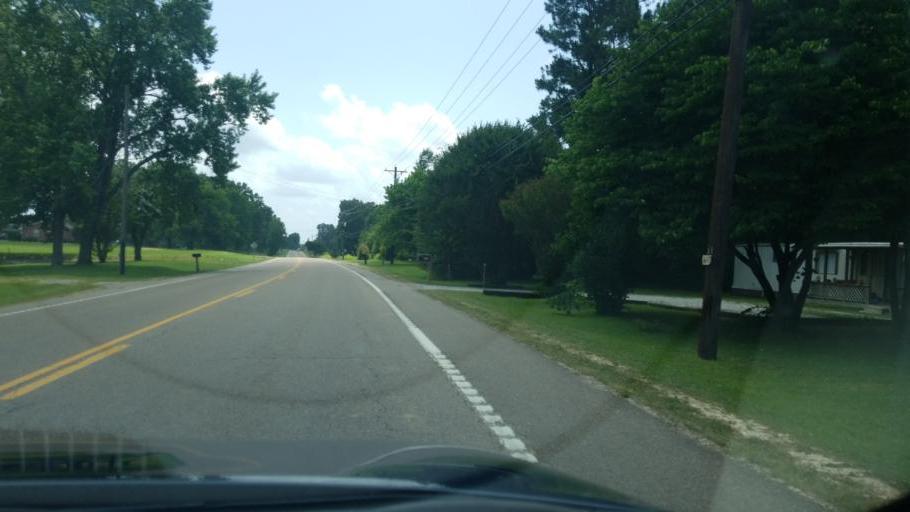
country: US
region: Tennessee
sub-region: Gibson County
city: Medina
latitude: 35.6957
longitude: -88.7313
